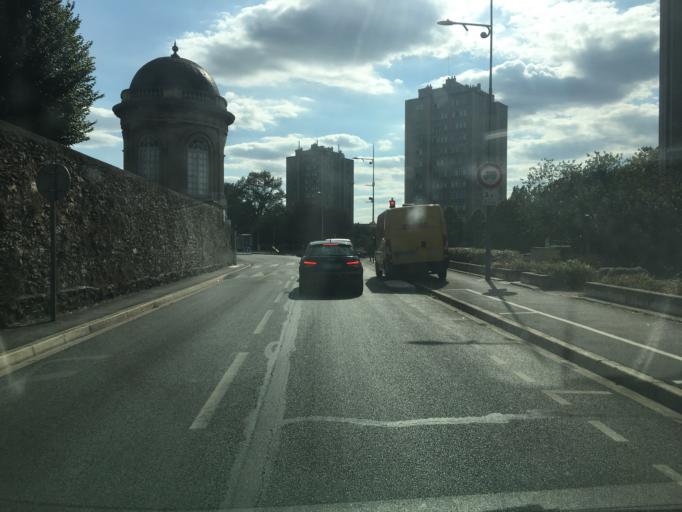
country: FR
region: Ile-de-France
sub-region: Departement du Val-de-Marne
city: Valenton
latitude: 48.7449
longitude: 2.4598
